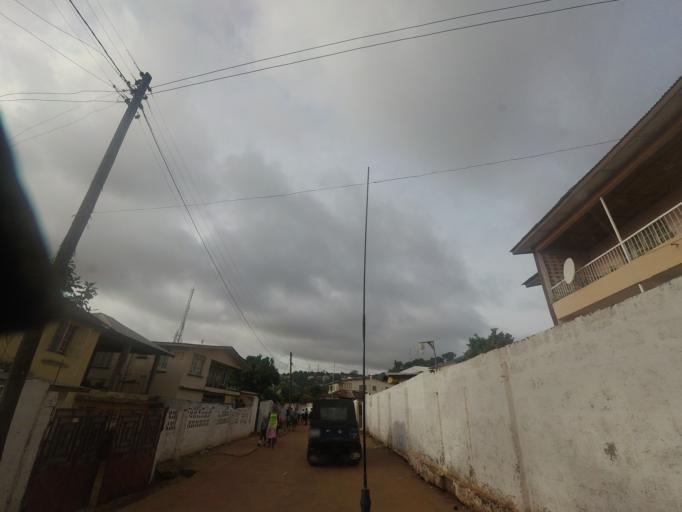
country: SL
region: Western Area
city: Freetown
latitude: 8.4880
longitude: -13.2648
